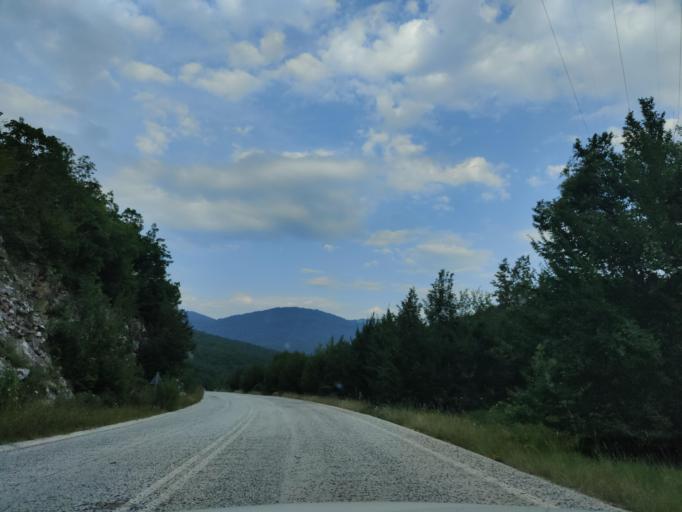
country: GR
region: East Macedonia and Thrace
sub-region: Nomos Dramas
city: Volakas
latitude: 41.2919
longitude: 23.9553
